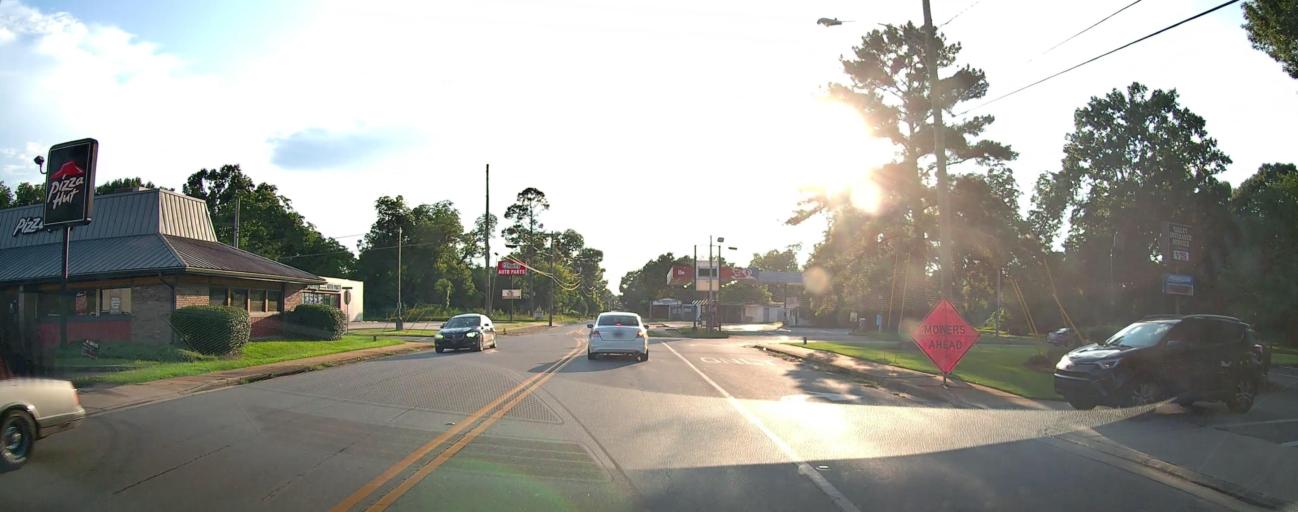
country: US
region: Georgia
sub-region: Peach County
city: Fort Valley
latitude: 32.5591
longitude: -83.8872
